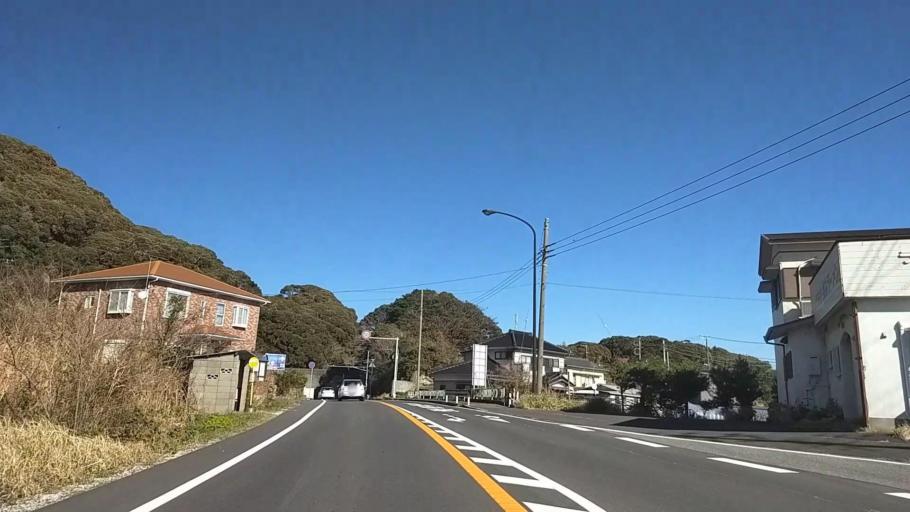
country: JP
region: Chiba
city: Kawaguchi
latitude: 35.0649
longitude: 140.0770
